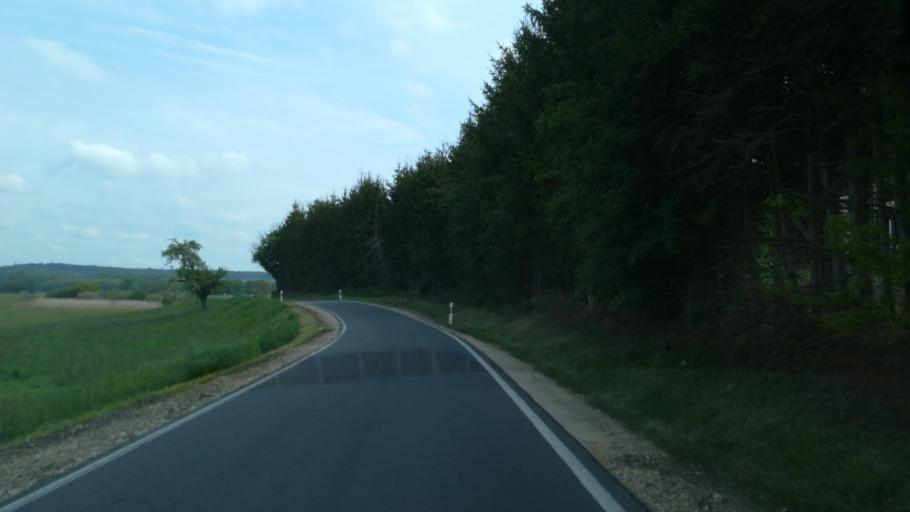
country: DE
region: Baden-Wuerttemberg
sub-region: Freiburg Region
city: Volkertshausen
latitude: 47.8002
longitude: 8.8861
